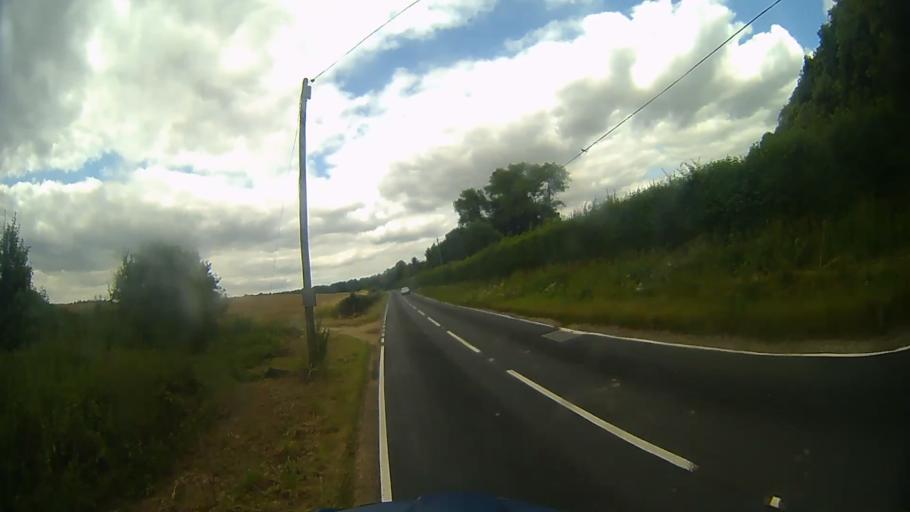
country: GB
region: England
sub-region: Hampshire
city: Four Marks
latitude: 51.1064
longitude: -1.1602
